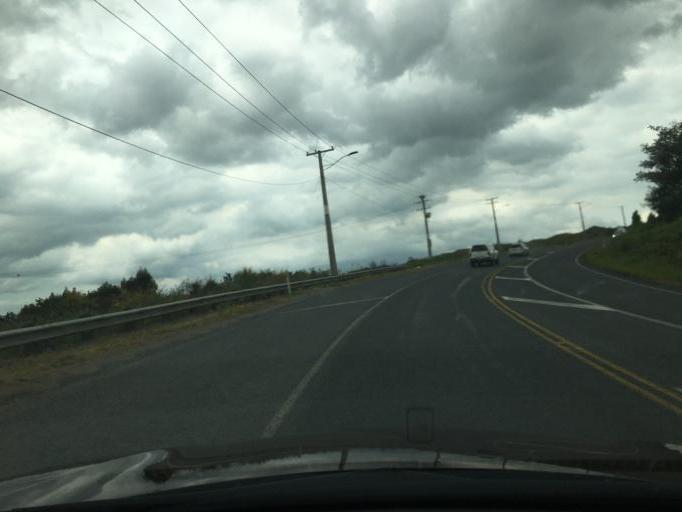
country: NZ
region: Waikato
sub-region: Waipa District
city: Cambridge
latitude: -37.8993
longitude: 175.4573
